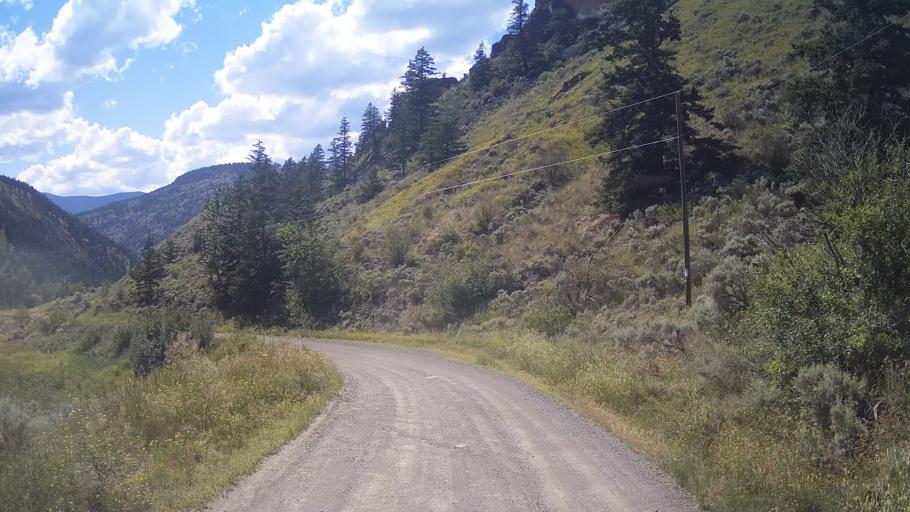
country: CA
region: British Columbia
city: Lillooet
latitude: 51.2255
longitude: -122.0680
